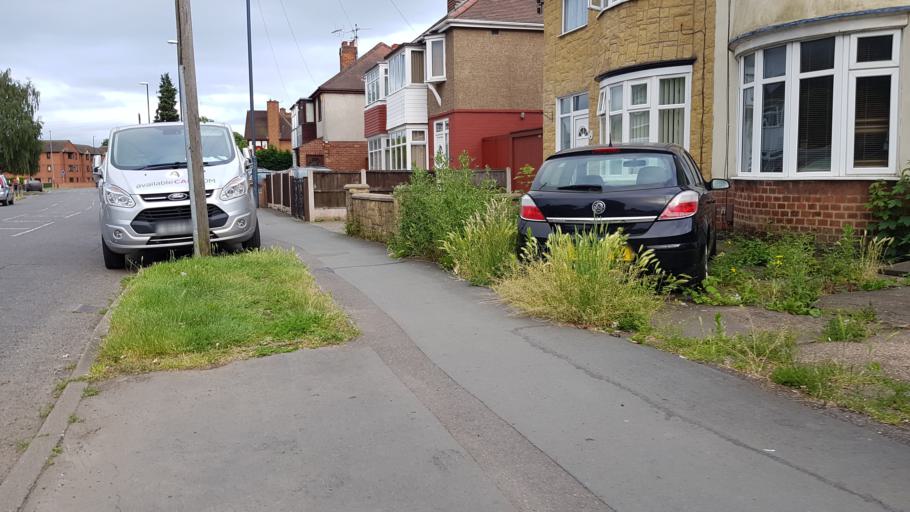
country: GB
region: England
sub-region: Derby
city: Derby
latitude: 52.8894
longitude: -1.4385
